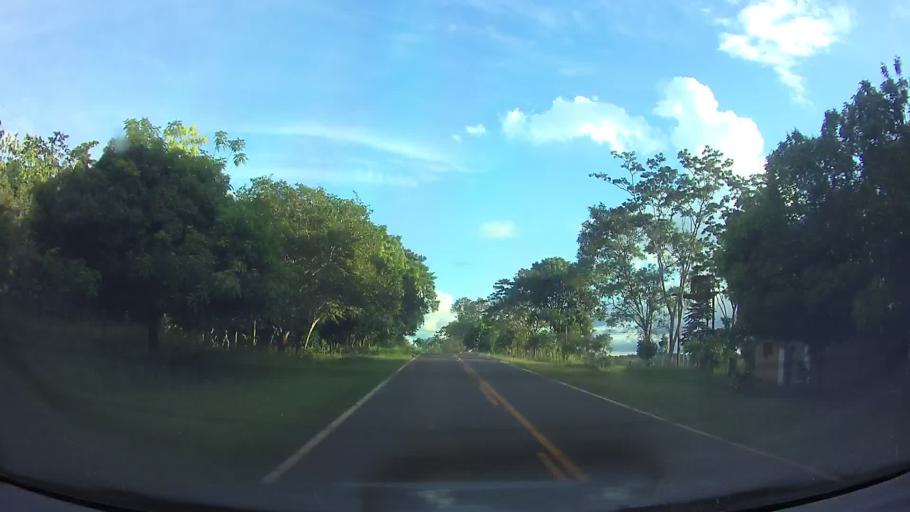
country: PY
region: Paraguari
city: Ybycui
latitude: -25.9582
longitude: -57.0900
